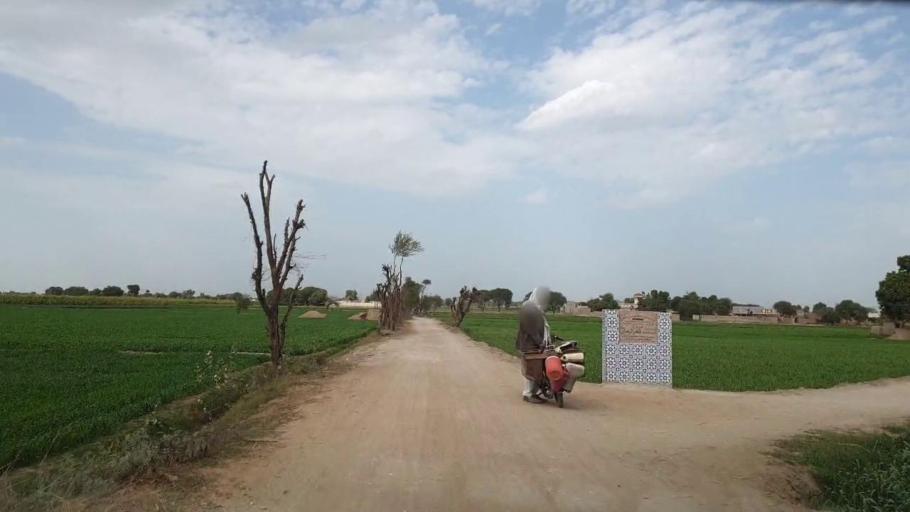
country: PK
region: Sindh
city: Tando Jam
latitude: 25.5456
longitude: 68.5861
